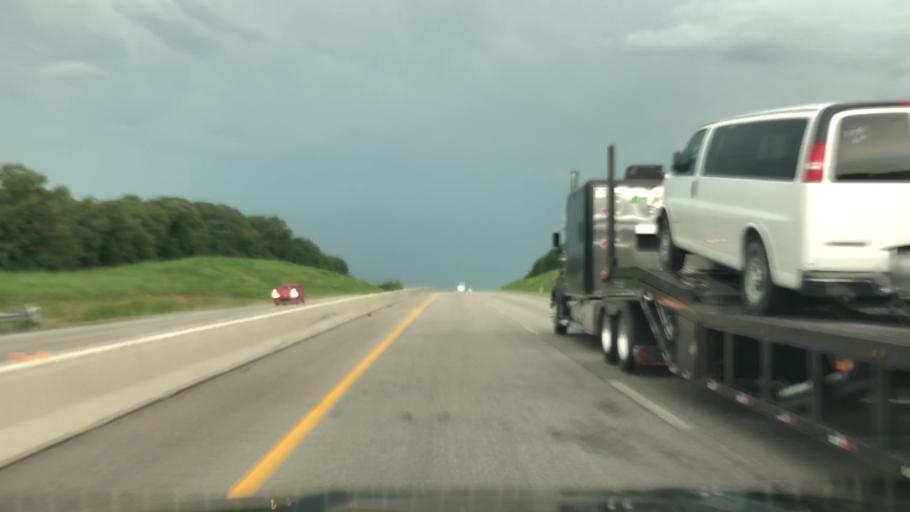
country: US
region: Oklahoma
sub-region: Rogers County
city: Justice
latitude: 36.3346
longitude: -95.5154
